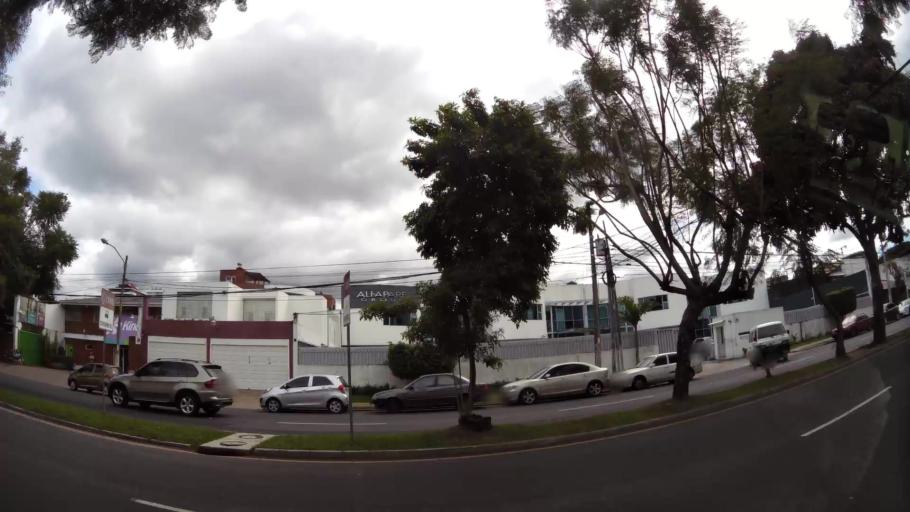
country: GT
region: Guatemala
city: Santa Catarina Pinula
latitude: 14.5809
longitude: -90.5241
